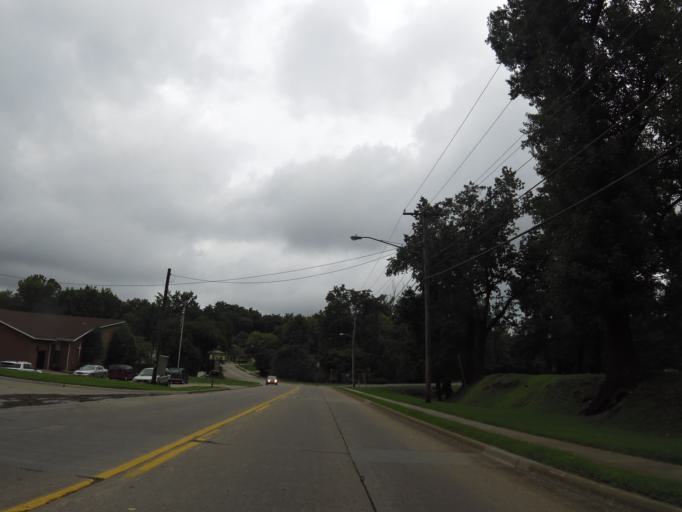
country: US
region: Missouri
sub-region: Cape Girardeau County
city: Cape Girardeau
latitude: 37.3323
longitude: -89.5459
